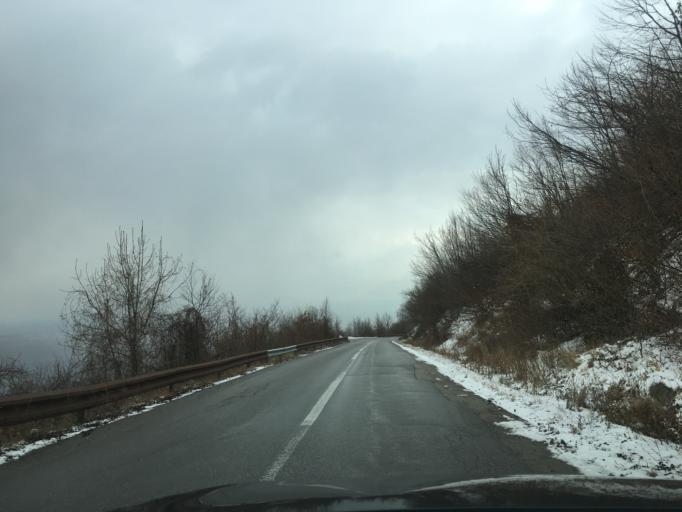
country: XK
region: Pec
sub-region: Komuna e Pejes
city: Dubova (Driloni)
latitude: 42.7538
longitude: 20.3007
